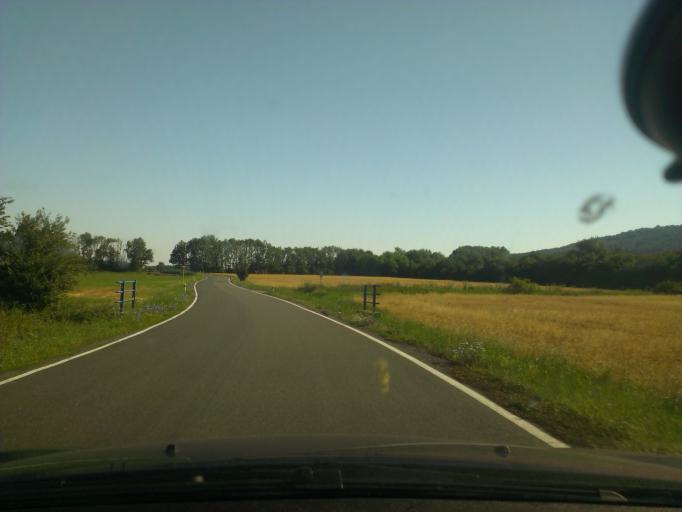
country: CZ
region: South Moravian
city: Velka nad Velickou
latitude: 48.8305
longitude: 17.5179
